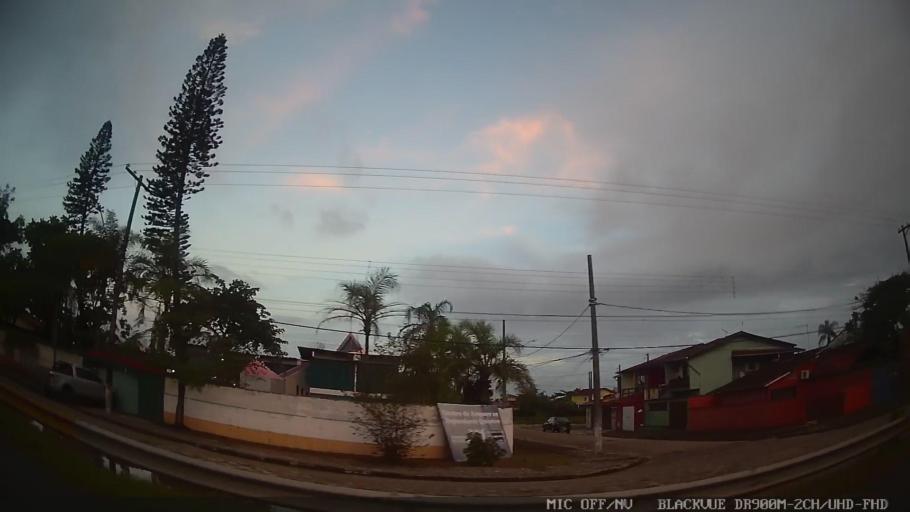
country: BR
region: Sao Paulo
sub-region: Mongagua
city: Mongagua
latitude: -24.1299
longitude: -46.6923
